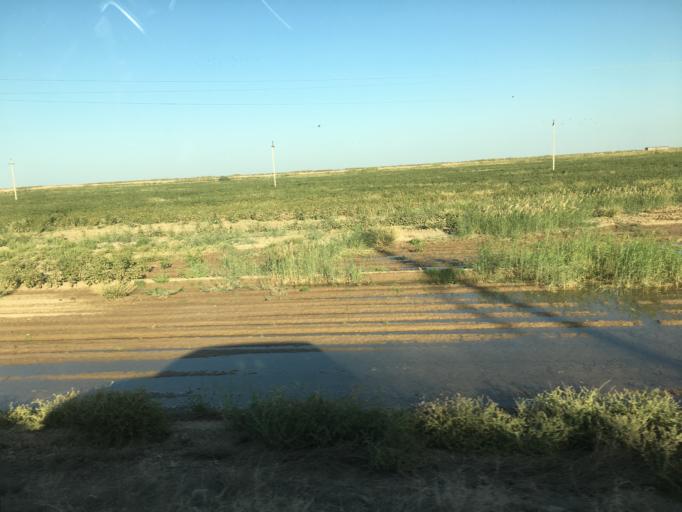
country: IR
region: Razavi Khorasan
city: Sarakhs
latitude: 37.1286
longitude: 61.2096
